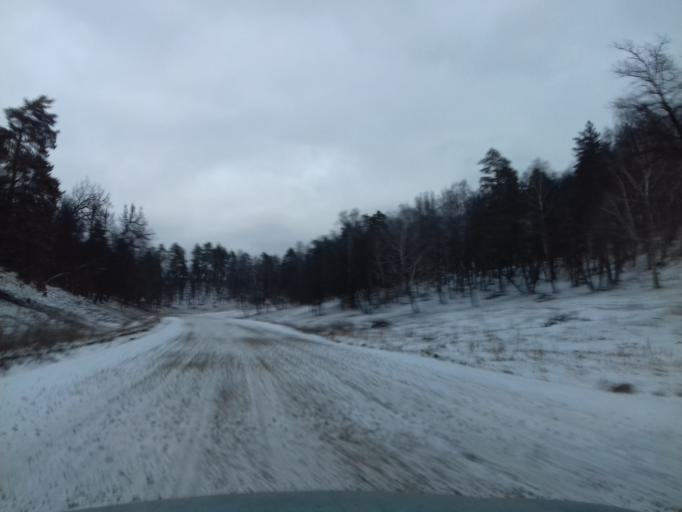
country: RU
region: Bashkortostan
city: Starosubkhangulovo
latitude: 53.0884
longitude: 57.4343
